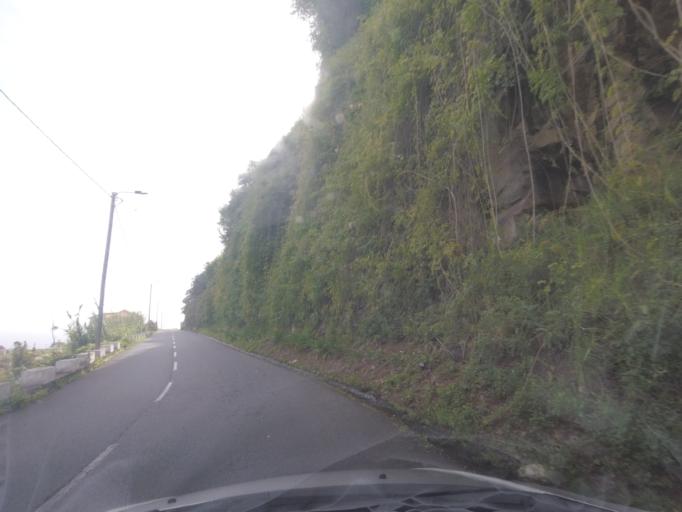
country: PT
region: Madeira
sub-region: Calheta
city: Estreito da Calheta
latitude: 32.7356
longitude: -17.1903
